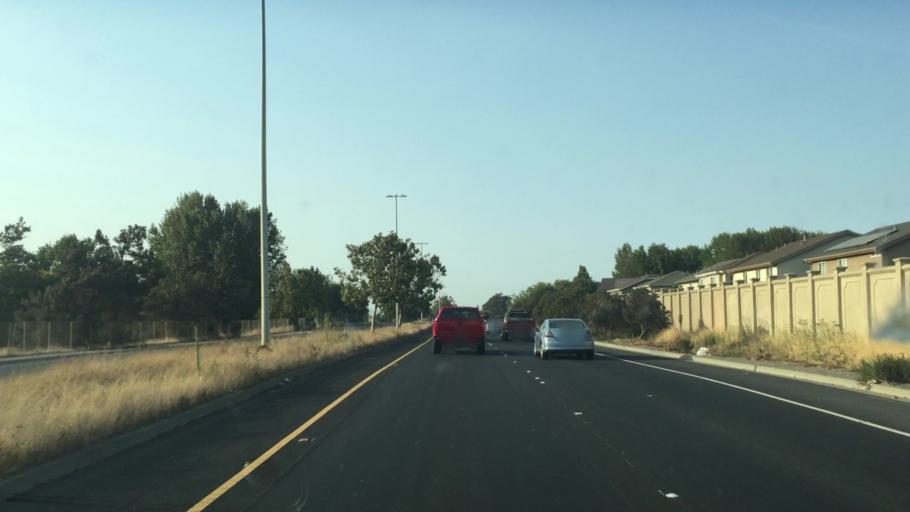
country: US
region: California
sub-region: Contra Costa County
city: North Richmond
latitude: 37.9563
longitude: -122.3736
